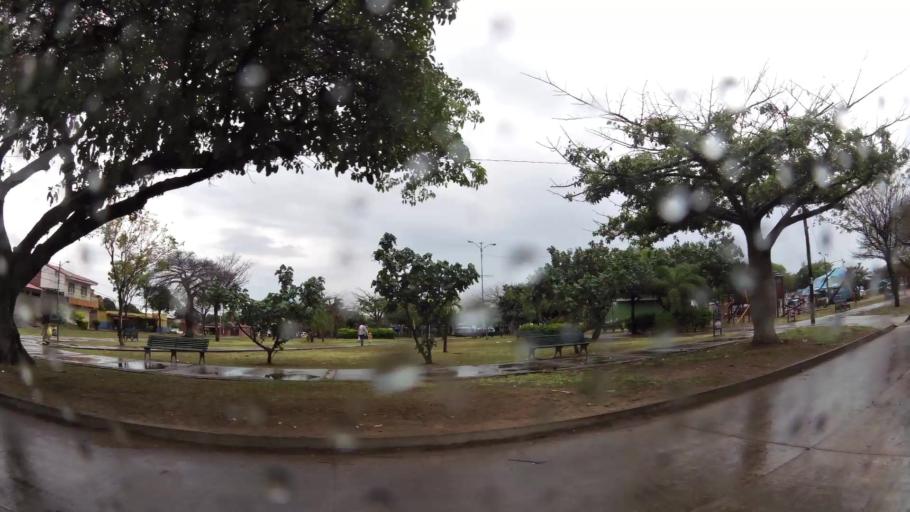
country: BO
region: Santa Cruz
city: Santa Cruz de la Sierra
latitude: -17.8001
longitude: -63.1544
